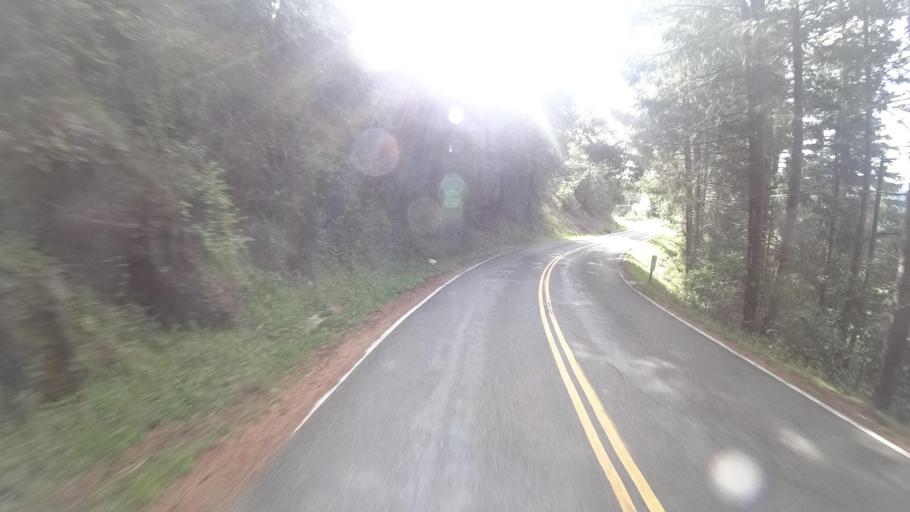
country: US
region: California
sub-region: Humboldt County
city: Bayside
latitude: 40.7483
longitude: -123.9694
